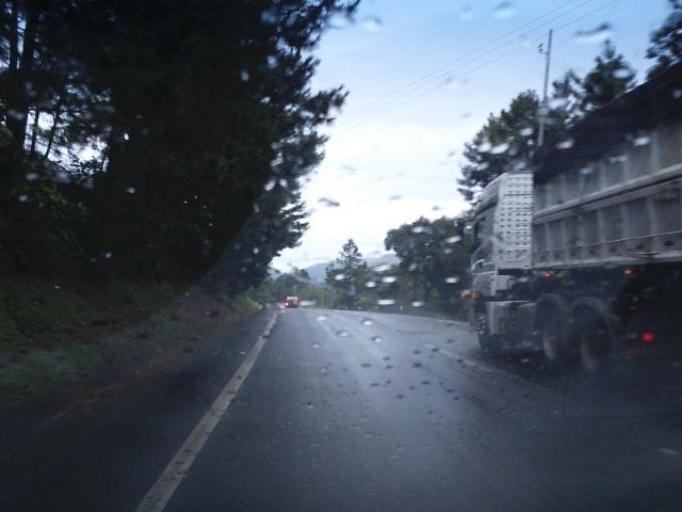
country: BR
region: Parana
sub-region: Sao Jose Dos Pinhais
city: Sao Jose dos Pinhais
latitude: -25.8536
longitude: -49.0282
